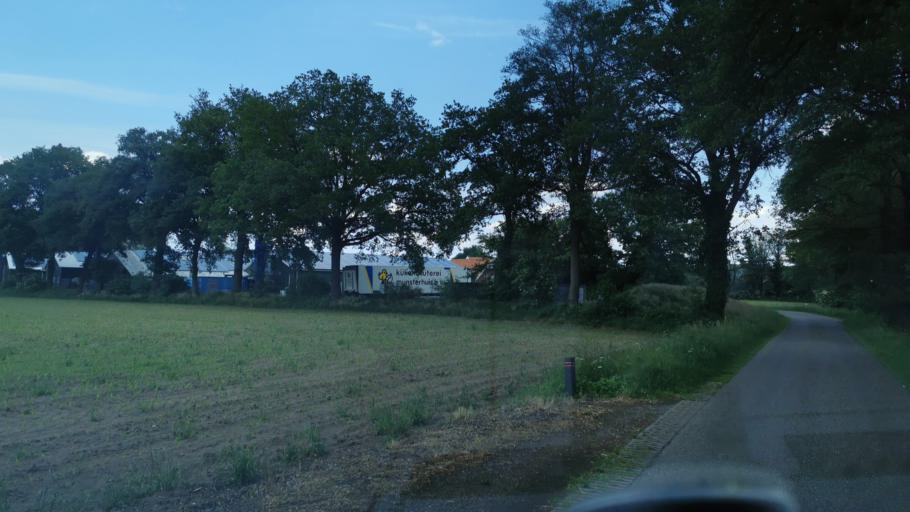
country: NL
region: Overijssel
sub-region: Gemeente Hengelo
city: Hengelo
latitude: 52.3284
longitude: 6.8361
